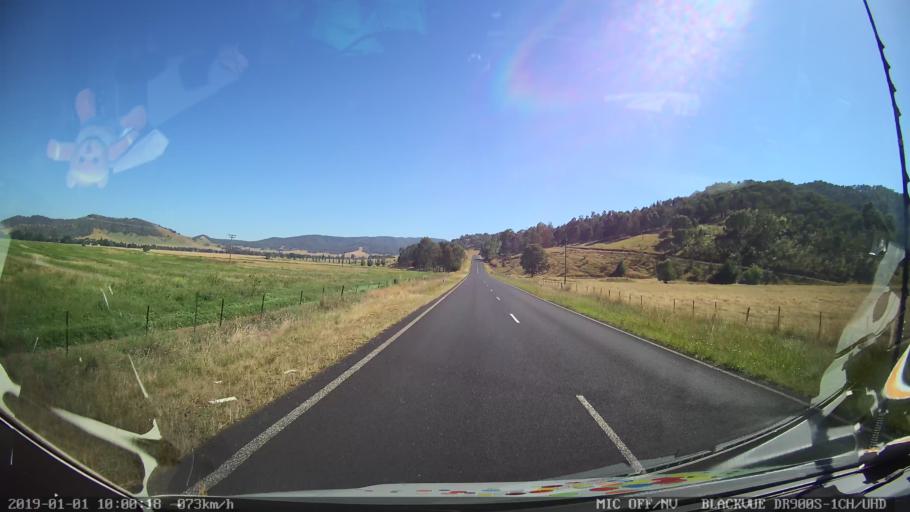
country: AU
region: New South Wales
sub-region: Snowy River
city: Jindabyne
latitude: -36.2038
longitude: 148.1019
